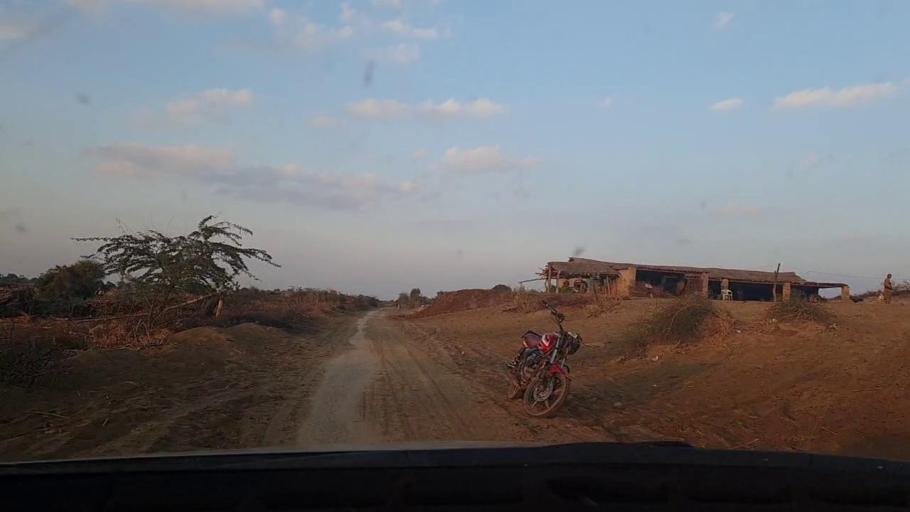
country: PK
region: Sindh
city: Tando Mittha Khan
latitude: 25.9387
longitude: 69.3374
